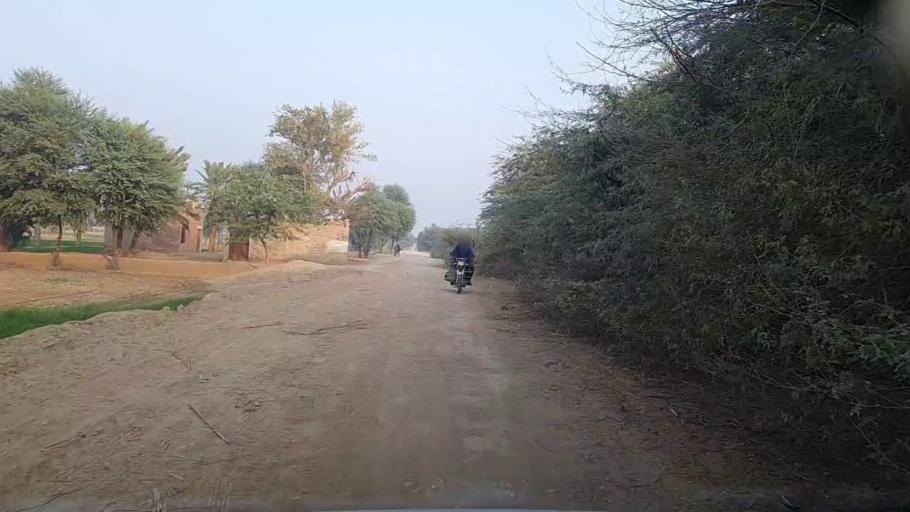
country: PK
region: Sindh
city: Bozdar
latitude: 27.0825
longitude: 68.5431
